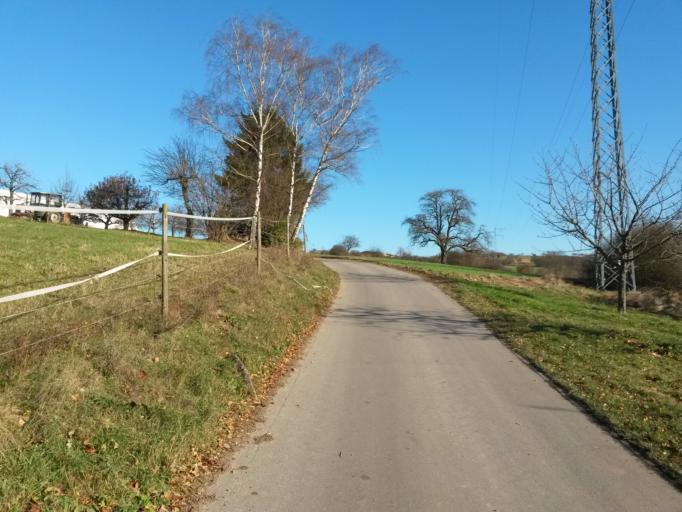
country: DE
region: Baden-Wuerttemberg
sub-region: Karlsruhe Region
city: Neuenburg
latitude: 48.8927
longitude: 8.5823
